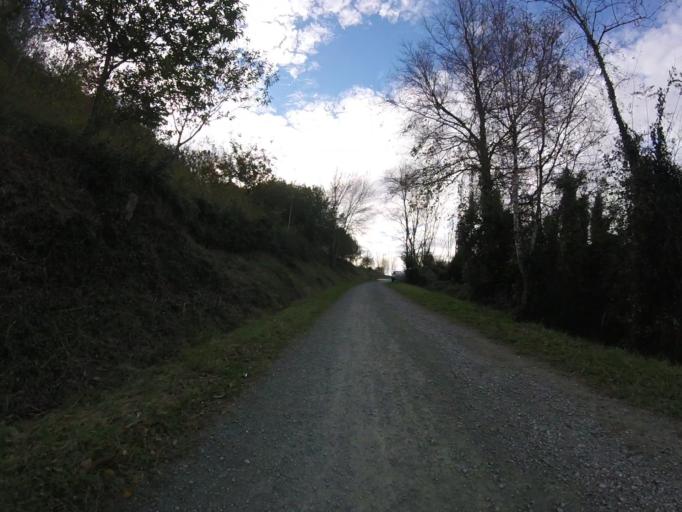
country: ES
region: Basque Country
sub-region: Provincia de Guipuzcoa
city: Errenteria
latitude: 43.2969
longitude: -1.9156
